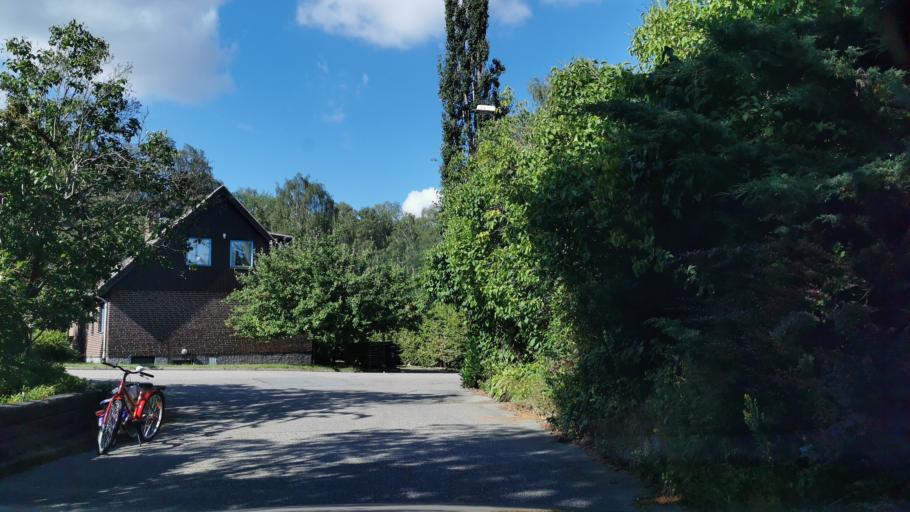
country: SE
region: Vaestra Goetaland
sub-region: Molndal
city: Moelndal
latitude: 57.6737
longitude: 11.9893
